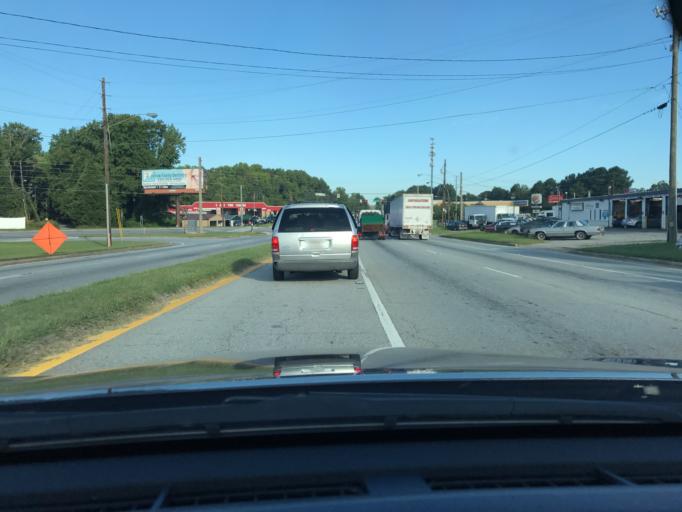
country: US
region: Georgia
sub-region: Clayton County
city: Lake City
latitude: 33.6138
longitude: -84.3480
